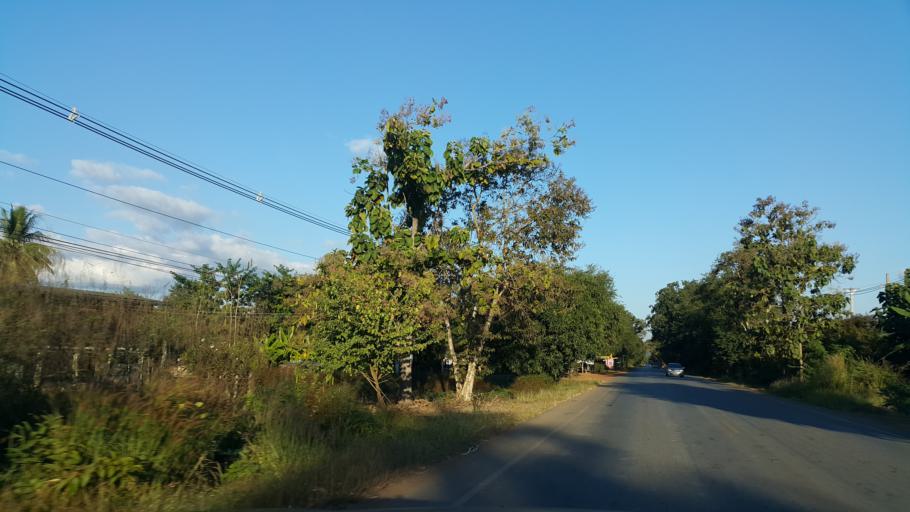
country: TH
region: Sukhothai
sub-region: Amphoe Si Satchanalai
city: Si Satchanalai
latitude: 17.5428
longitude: 99.8264
